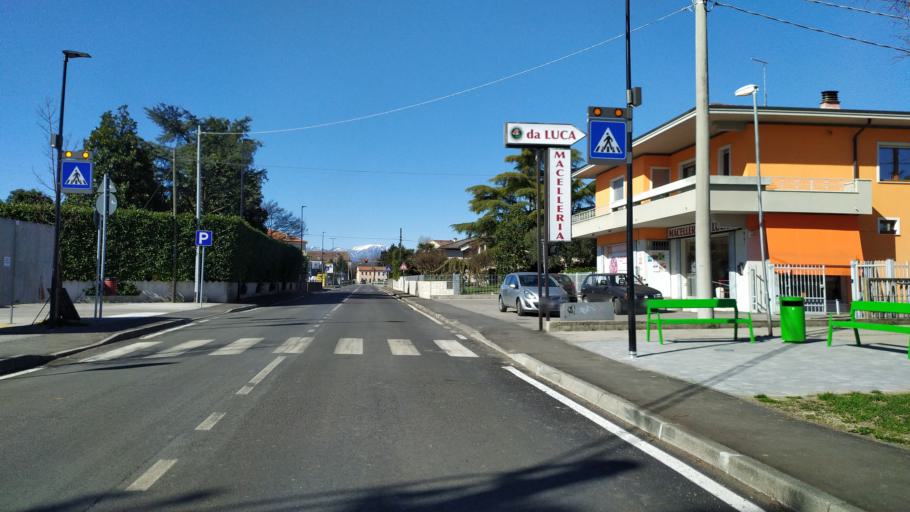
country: IT
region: Veneto
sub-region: Provincia di Vicenza
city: Vigardolo
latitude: 45.6064
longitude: 11.5893
